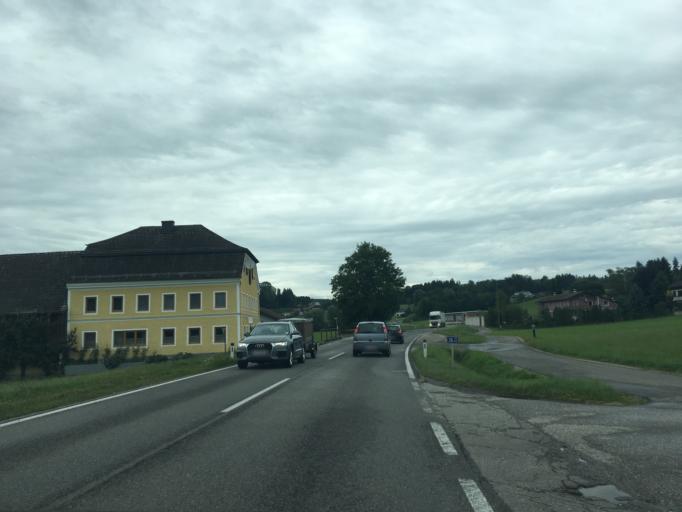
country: AT
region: Salzburg
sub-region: Politischer Bezirk Salzburg-Umgebung
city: Dorfbeuern
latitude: 48.0625
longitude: 12.9875
